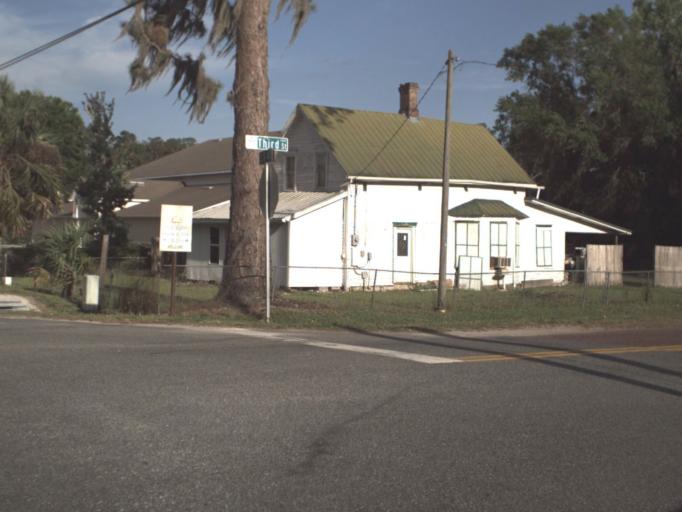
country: US
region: Florida
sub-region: Lake County
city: Astor
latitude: 29.1625
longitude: -81.5308
